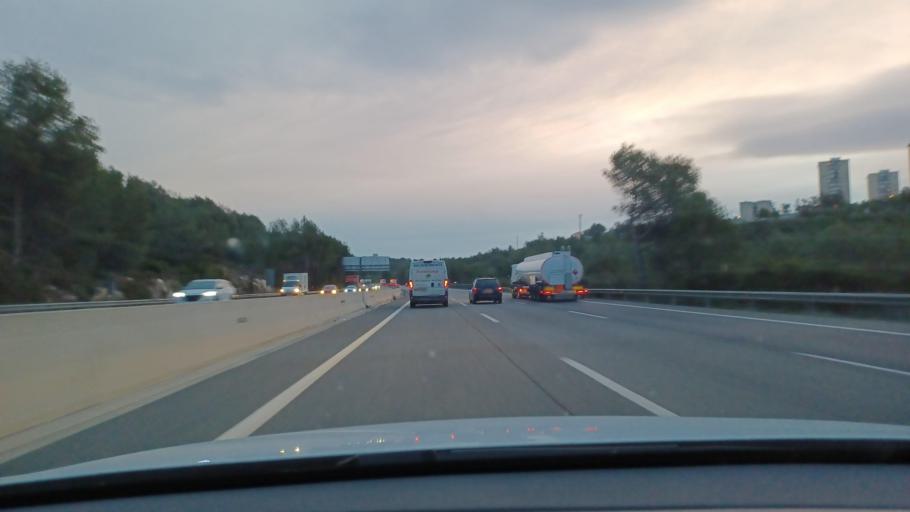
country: ES
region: Catalonia
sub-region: Provincia de Tarragona
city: Tarragona
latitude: 41.1434
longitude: 1.2486
